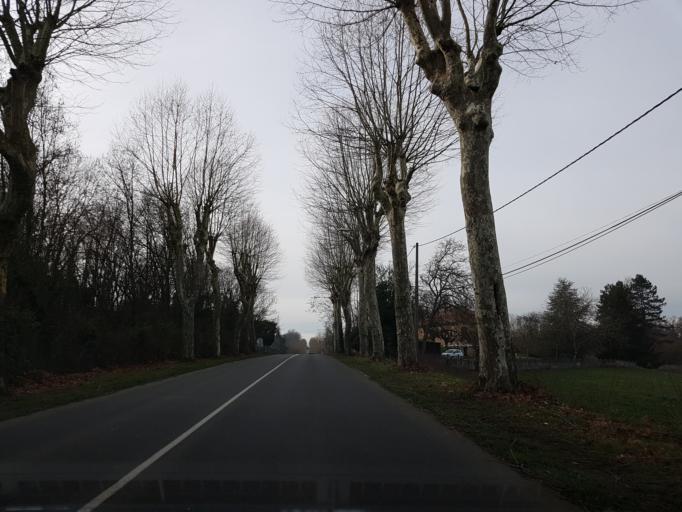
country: FR
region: Auvergne
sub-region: Departement de l'Allier
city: Neuvy
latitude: 46.5575
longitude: 3.3062
